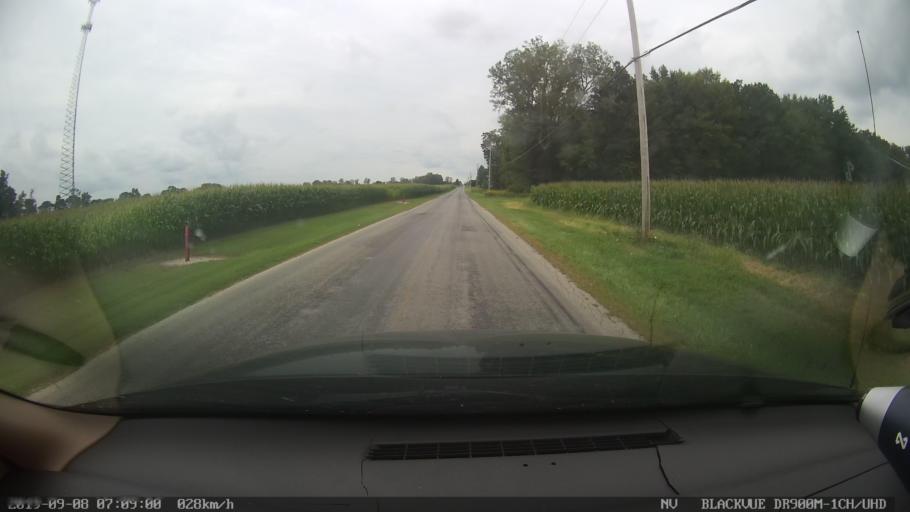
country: US
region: Ohio
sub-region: Richland County
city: Shelby
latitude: 40.9085
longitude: -82.6647
